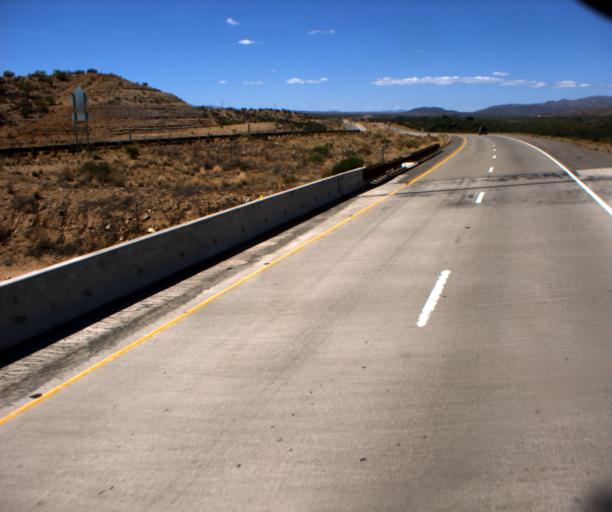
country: US
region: Arizona
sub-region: Yavapai County
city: Bagdad
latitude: 34.8196
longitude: -113.6261
